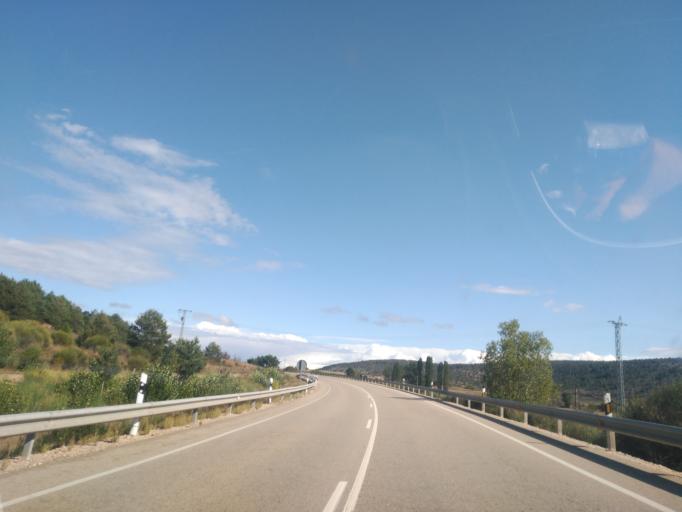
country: ES
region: Castille and Leon
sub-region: Provincia de Burgos
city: Hontoria del Pinar
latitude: 41.8557
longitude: -3.1922
